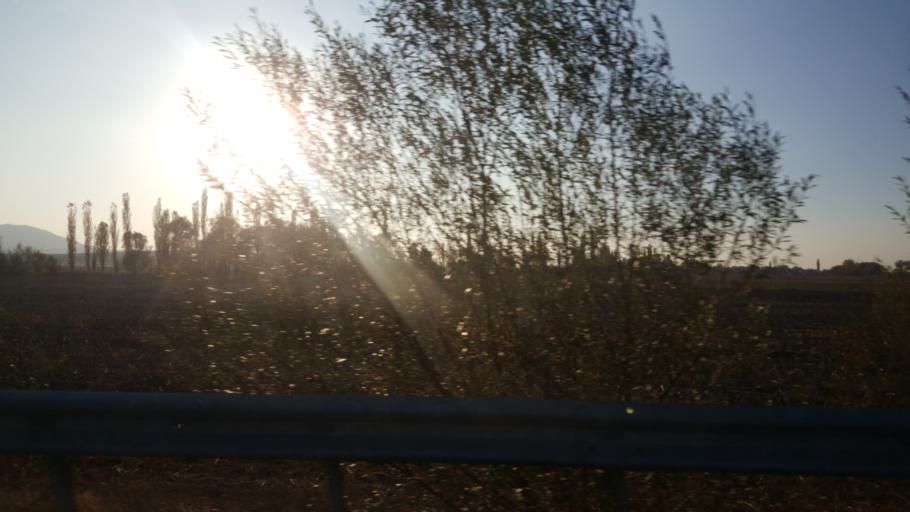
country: TR
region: Eskisehir
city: Mahmudiye
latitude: 39.5717
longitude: 30.9119
